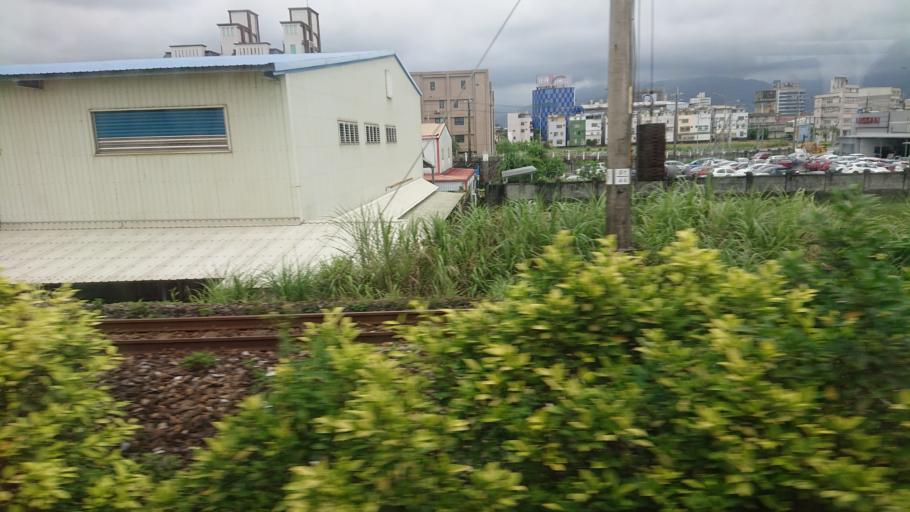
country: TW
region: Taiwan
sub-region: Yilan
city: Yilan
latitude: 24.7656
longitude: 121.7624
